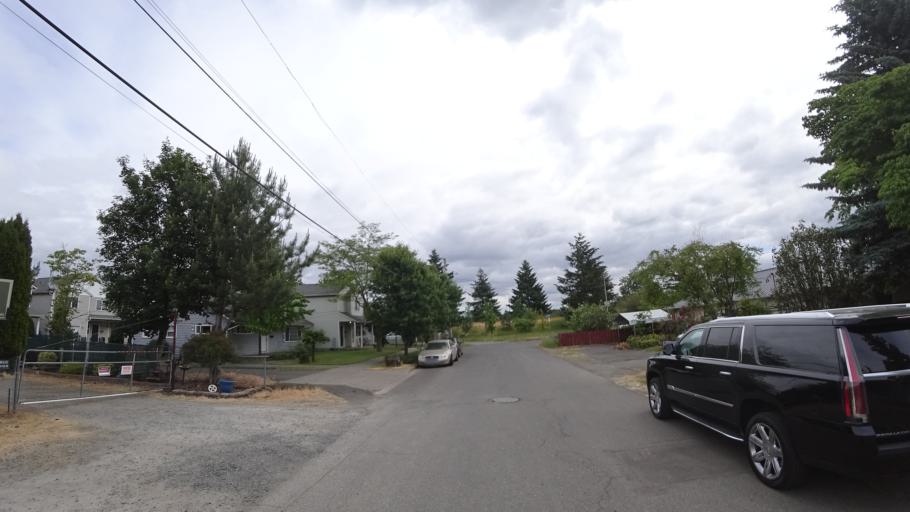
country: US
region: Oregon
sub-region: Multnomah County
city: Lents
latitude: 45.4889
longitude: -122.5679
